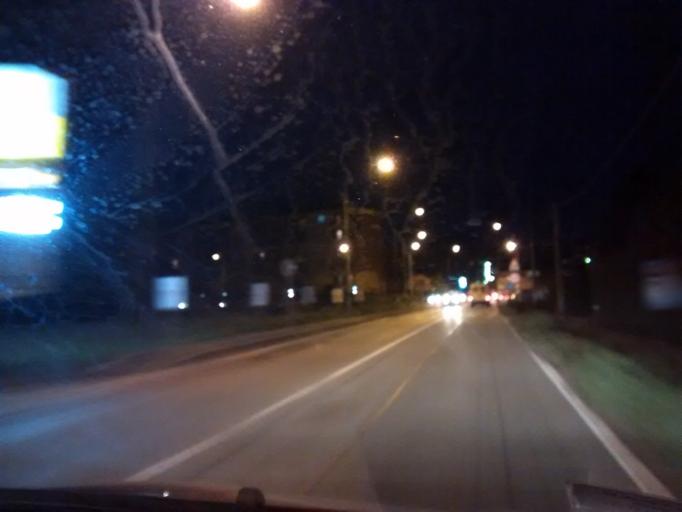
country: IT
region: Piedmont
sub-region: Provincia di Torino
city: Pinerolo
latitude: 44.8753
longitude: 7.3334
